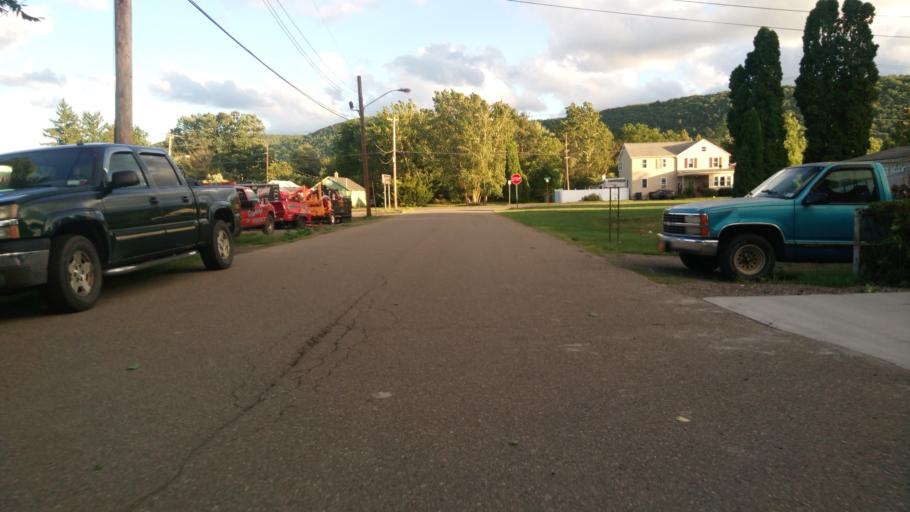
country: US
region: New York
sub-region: Chemung County
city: Southport
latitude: 42.0592
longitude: -76.7984
